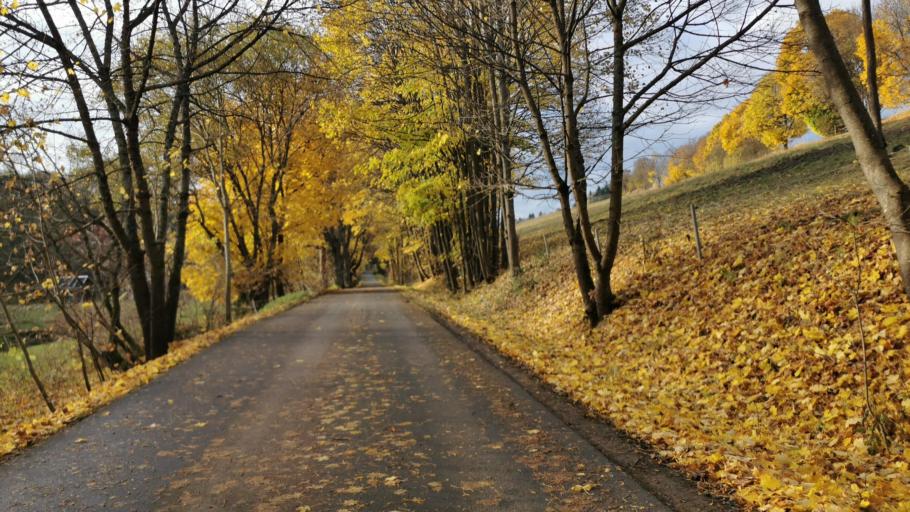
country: DE
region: Thuringia
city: Wurzbach
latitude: 50.4509
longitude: 11.5448
